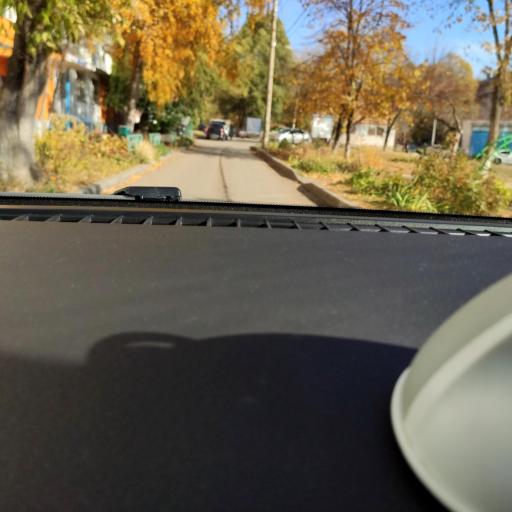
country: RU
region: Samara
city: Samara
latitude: 53.2518
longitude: 50.2277
